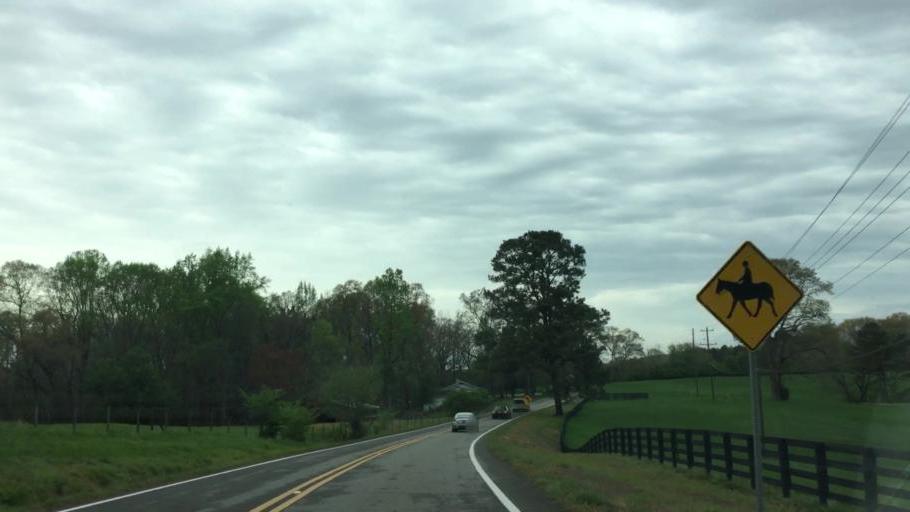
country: US
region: Georgia
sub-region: Fulton County
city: Milton
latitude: 34.1848
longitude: -84.3407
